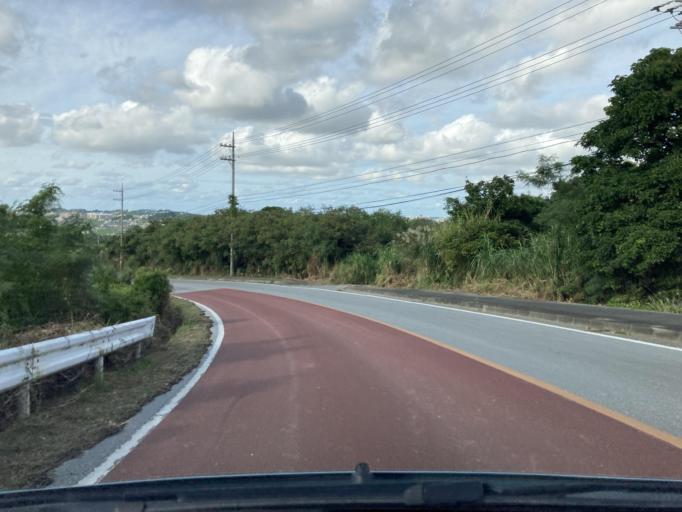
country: JP
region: Okinawa
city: Itoman
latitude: 26.1292
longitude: 127.7128
